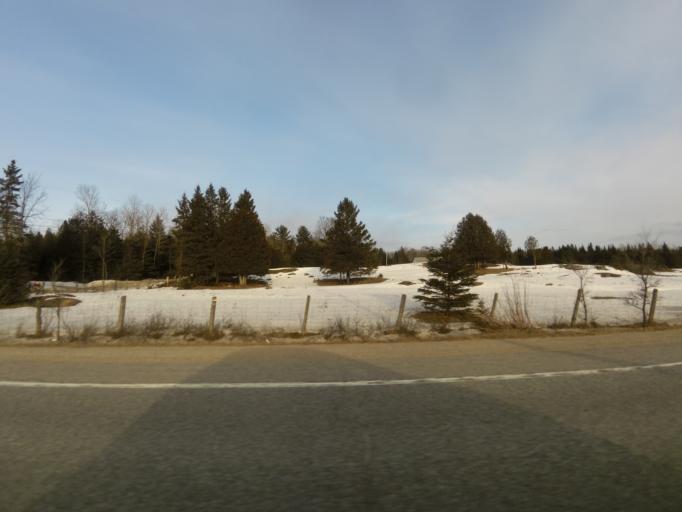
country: CA
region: Quebec
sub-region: Outaouais
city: Wakefield
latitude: 45.8996
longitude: -76.0253
